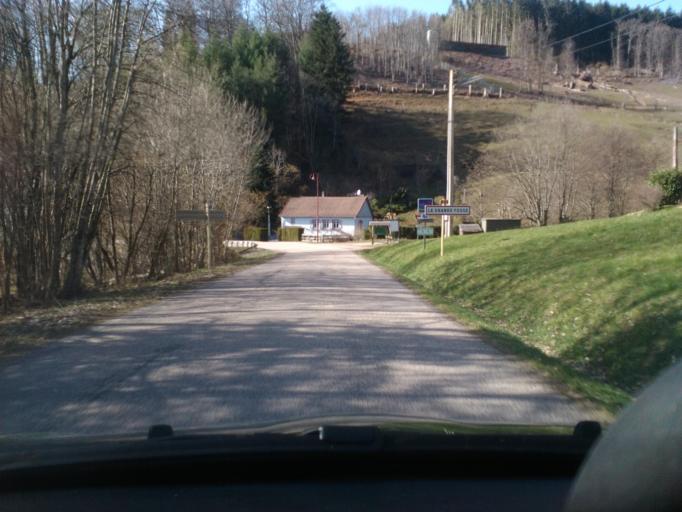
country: FR
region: Lorraine
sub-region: Departement des Vosges
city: Ban-de-Laveline
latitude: 48.3421
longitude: 7.0735
